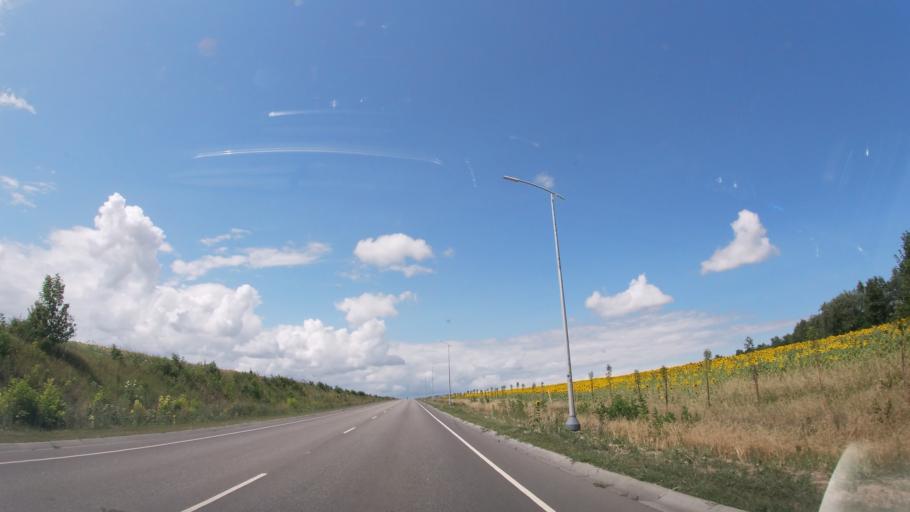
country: RU
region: Belgorod
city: Severnyy
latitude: 50.6646
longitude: 36.5167
